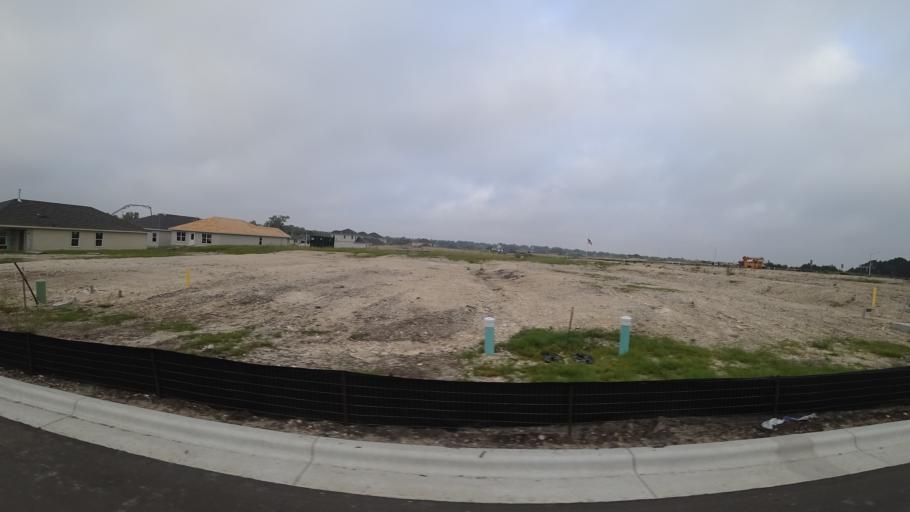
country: US
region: Texas
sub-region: Travis County
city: Wells Branch
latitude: 30.3569
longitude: -97.6624
